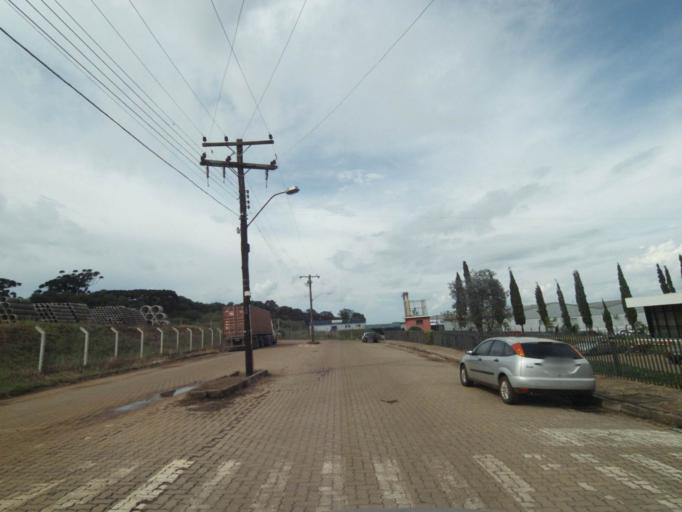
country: BR
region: Rio Grande do Sul
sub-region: Lagoa Vermelha
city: Lagoa Vermelha
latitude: -28.2276
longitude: -51.5098
